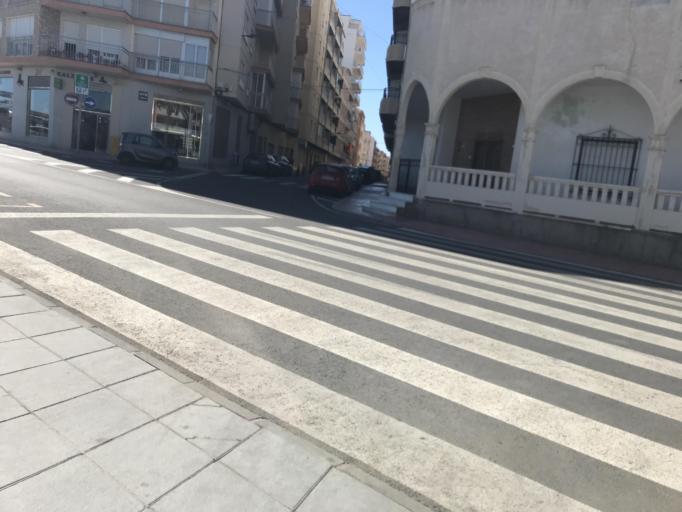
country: ES
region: Valencia
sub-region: Provincia de Alicante
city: Torrevieja
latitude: 37.9767
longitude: -0.6711
